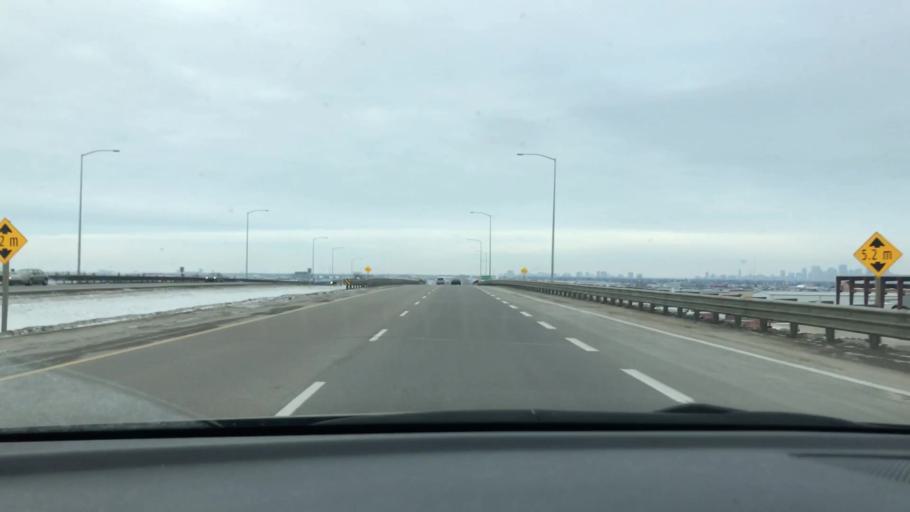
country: CA
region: Alberta
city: Sherwood Park
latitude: 53.5174
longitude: -113.3831
